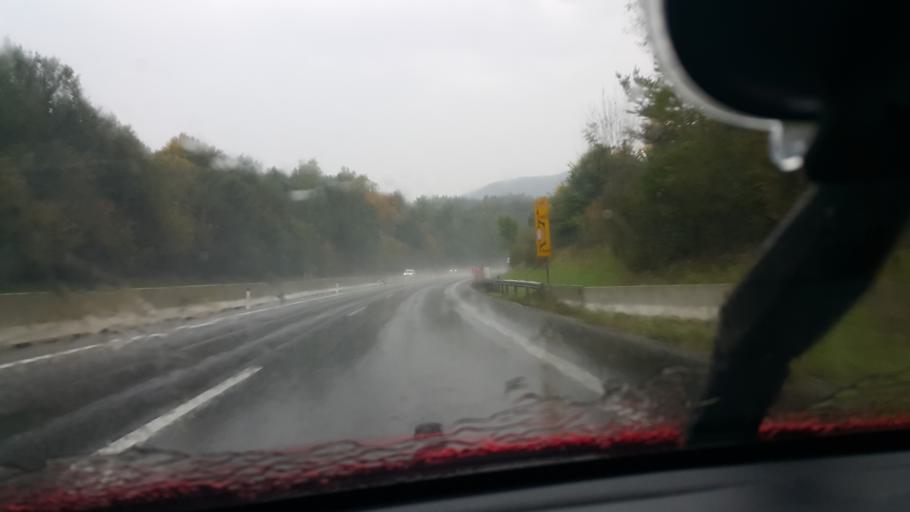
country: AT
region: Carinthia
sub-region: Politischer Bezirk Volkermarkt
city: Voelkermarkt
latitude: 46.6737
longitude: 14.5882
